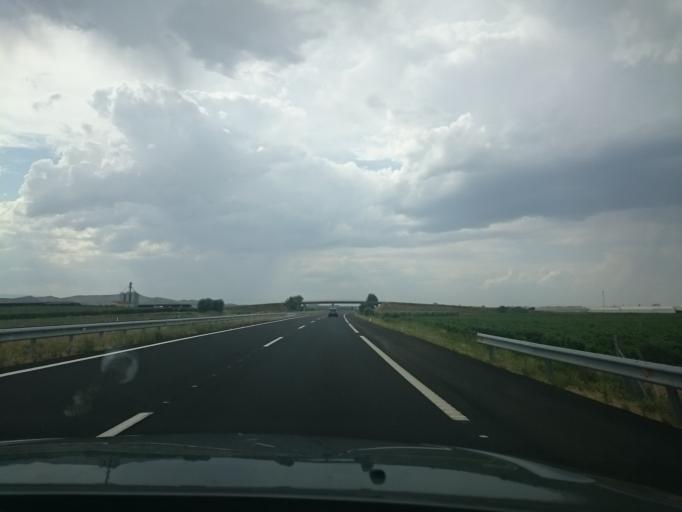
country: ES
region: La Rioja
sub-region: Provincia de La Rioja
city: Aldeanueva de Ebro
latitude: 42.2162
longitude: -1.8884
